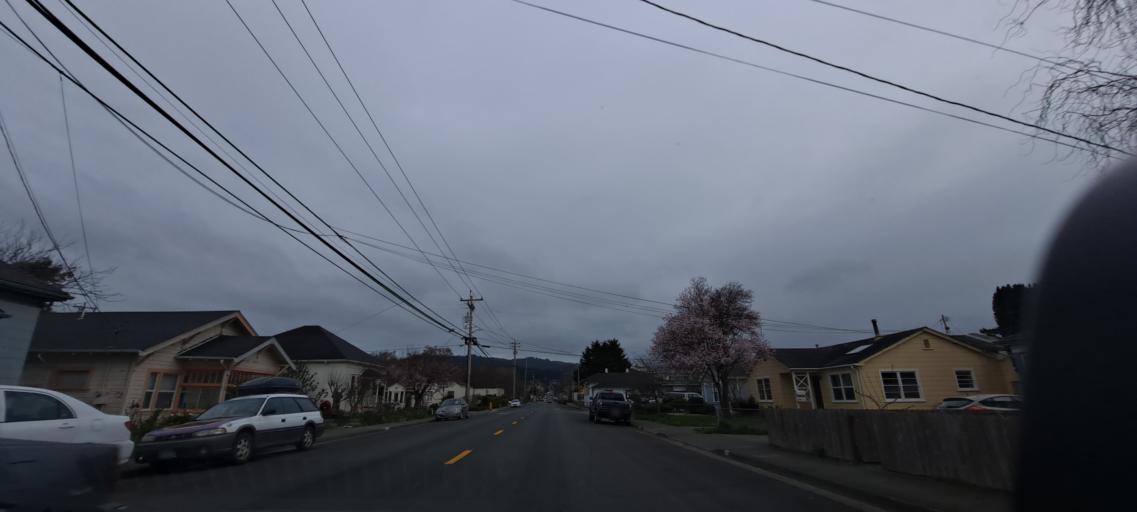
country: US
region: California
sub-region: Humboldt County
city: Arcata
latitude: 40.8724
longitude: -124.0943
